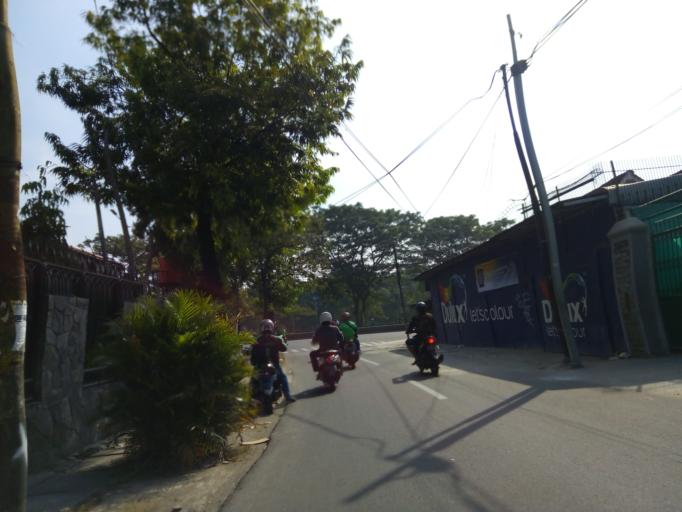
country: ID
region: Jakarta Raya
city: Jakarta
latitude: -6.2066
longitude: 106.8377
